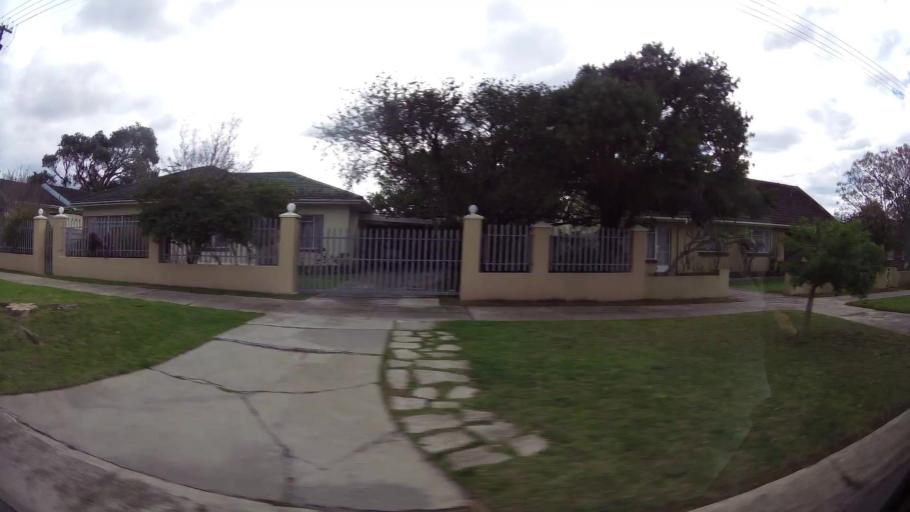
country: ZA
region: Eastern Cape
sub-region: Nelson Mandela Bay Metropolitan Municipality
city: Port Elizabeth
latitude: -33.9428
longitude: 25.5185
